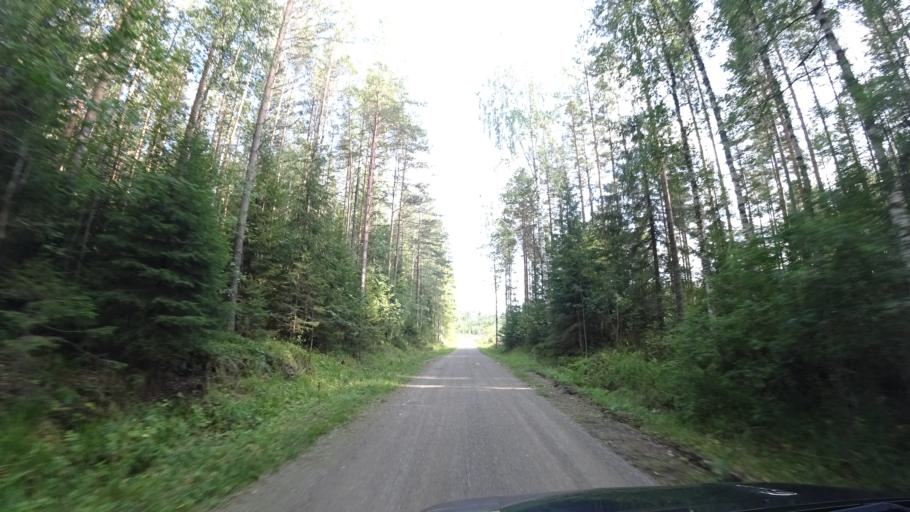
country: FI
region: Paijanne Tavastia
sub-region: Lahti
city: Auttoinen
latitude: 61.2183
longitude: 25.1507
